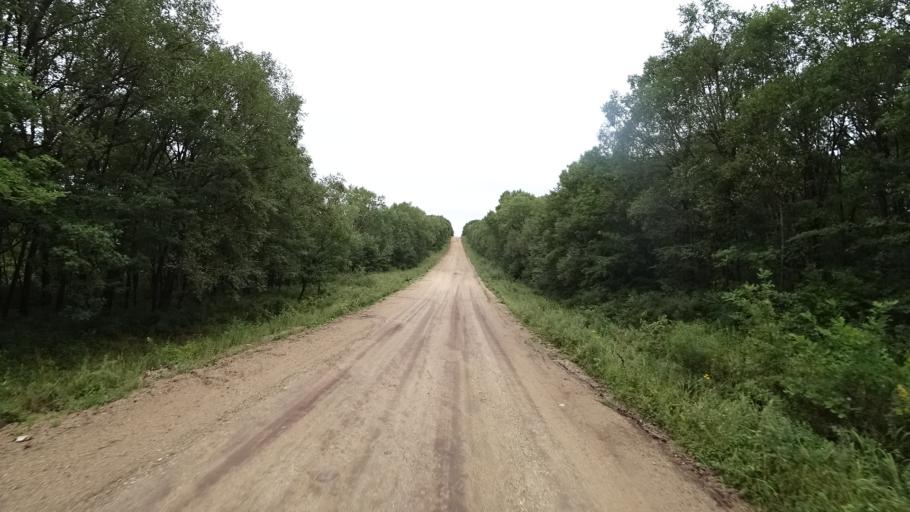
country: RU
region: Primorskiy
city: Ivanovka
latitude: 44.0450
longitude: 132.5434
